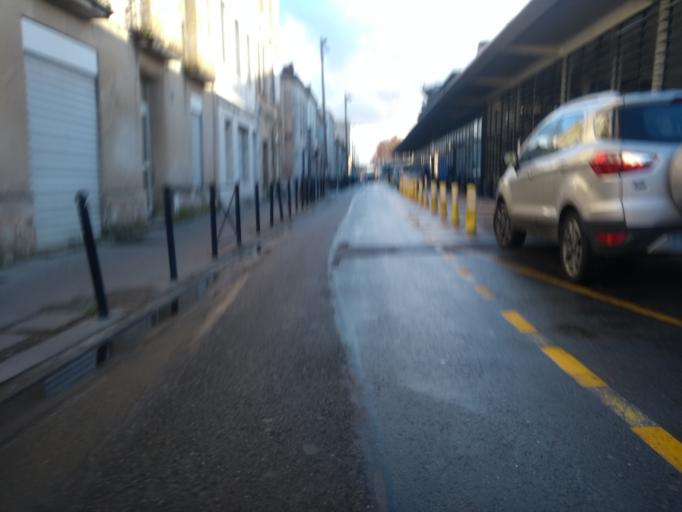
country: FR
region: Aquitaine
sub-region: Departement de la Gironde
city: Begles
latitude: 44.8253
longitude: -0.5546
